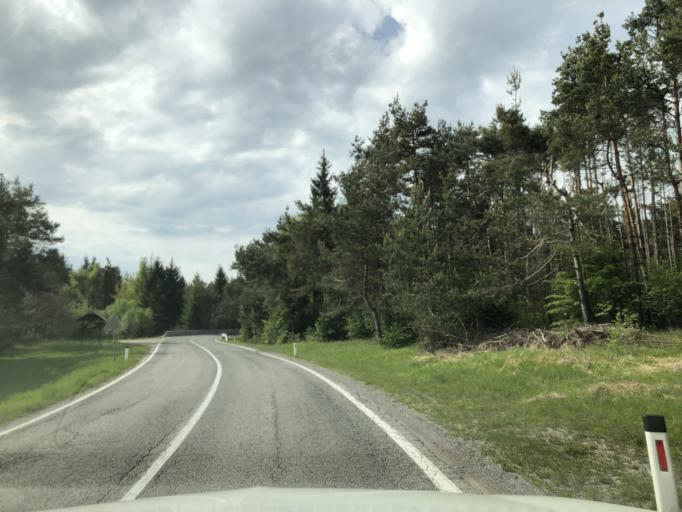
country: SI
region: Bloke
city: Nova Vas
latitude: 45.7682
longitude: 14.4814
